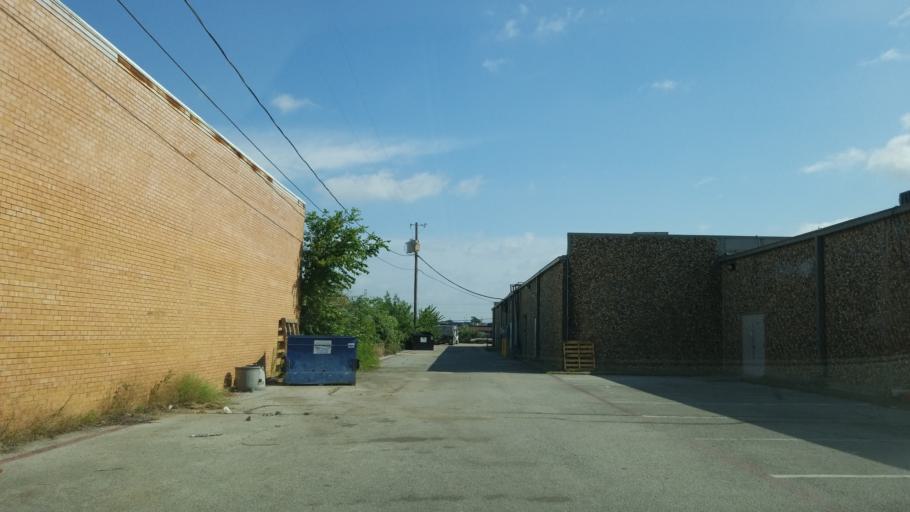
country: US
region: Texas
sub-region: Dallas County
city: Farmers Branch
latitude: 32.8795
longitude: -96.8893
